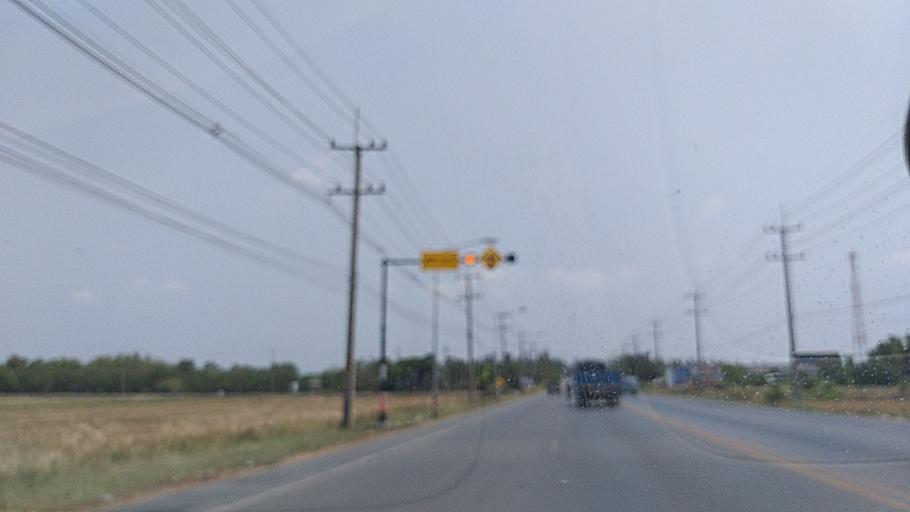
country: TH
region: Bangkok
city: Nong Chok
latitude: 13.9695
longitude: 100.9561
